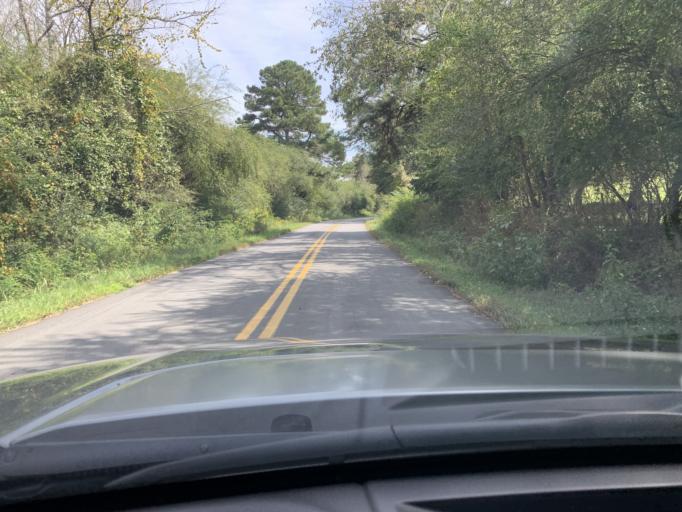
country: US
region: Georgia
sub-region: Polk County
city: Cedartown
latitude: 33.9478
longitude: -85.3669
